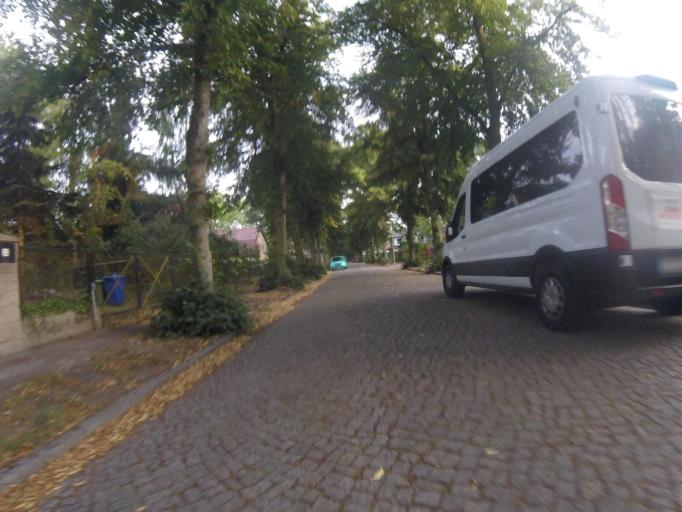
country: DE
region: Brandenburg
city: Zeuthen
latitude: 52.3547
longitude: 13.6203
